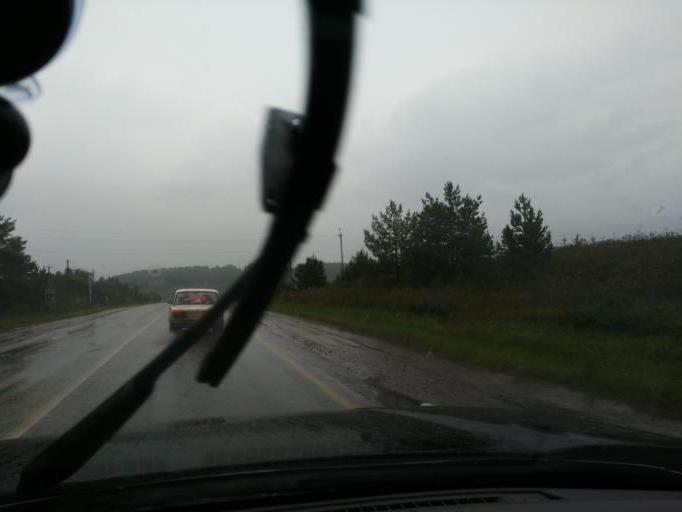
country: RU
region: Perm
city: Osa
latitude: 57.1944
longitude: 55.5916
